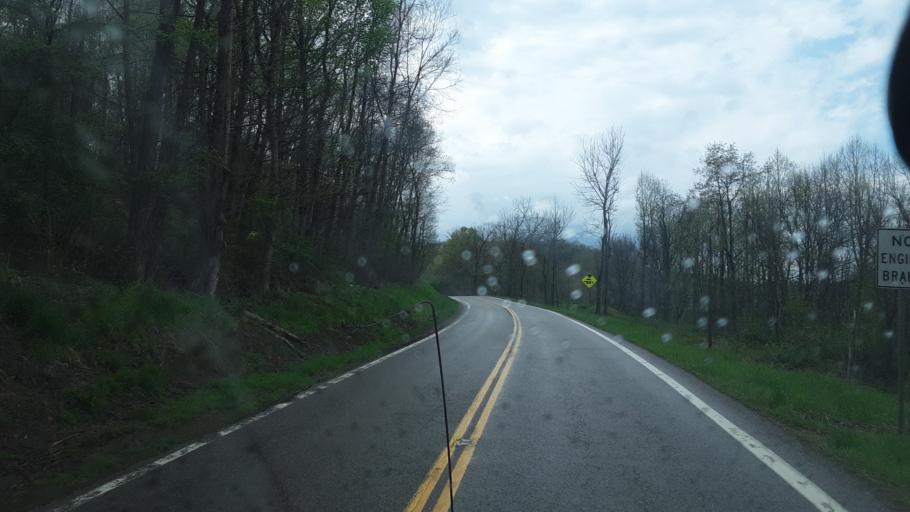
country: US
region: Ohio
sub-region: Guernsey County
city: Mantua
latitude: 40.0733
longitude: -81.7561
